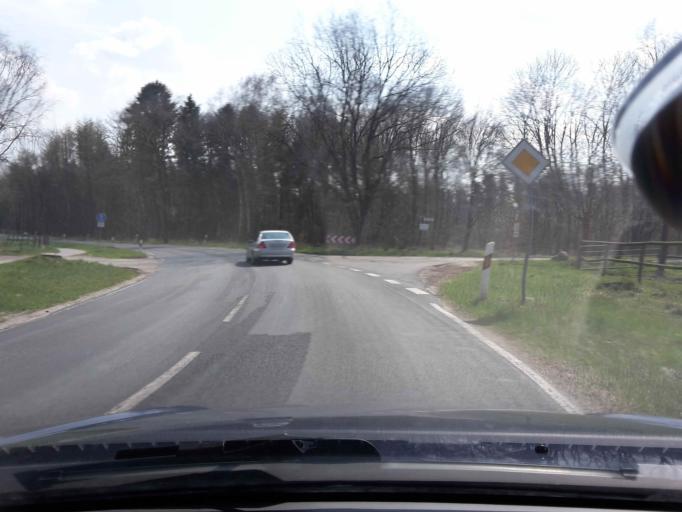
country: DE
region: Lower Saxony
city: Buchholz in der Nordheide
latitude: 53.3158
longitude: 9.8992
